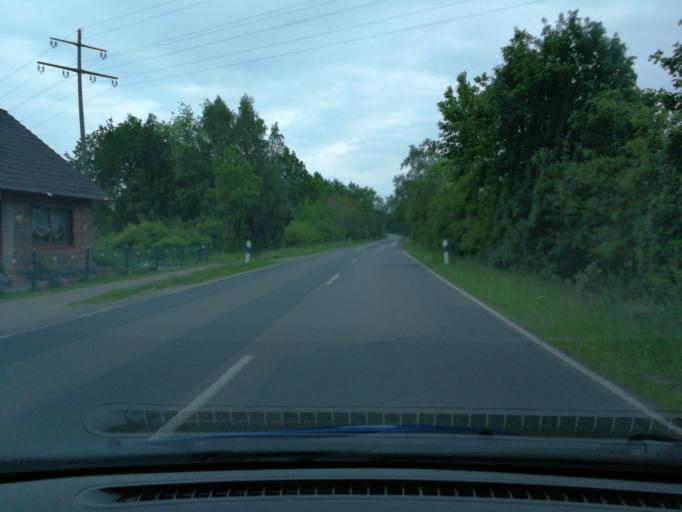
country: DE
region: Schleswig-Holstein
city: Siebeneichen
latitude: 53.5024
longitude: 10.6135
